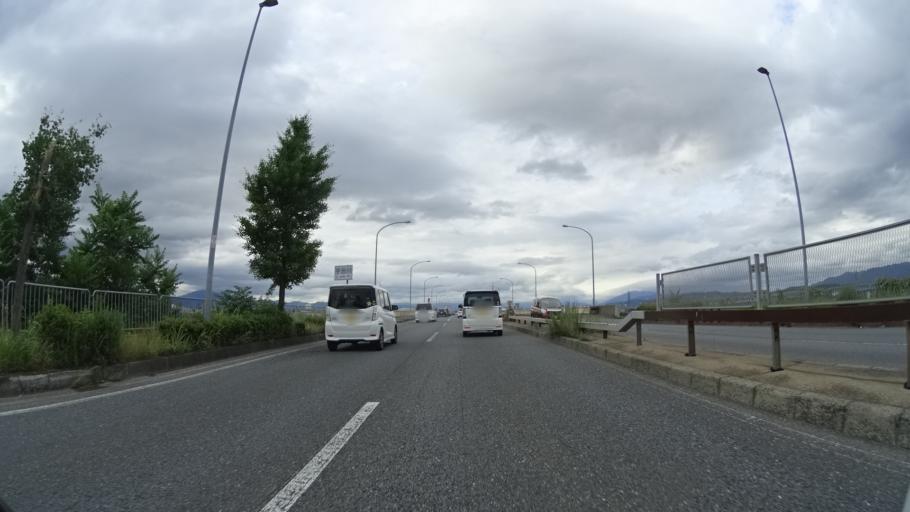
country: JP
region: Kyoto
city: Yawata
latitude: 34.9145
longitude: 135.7445
